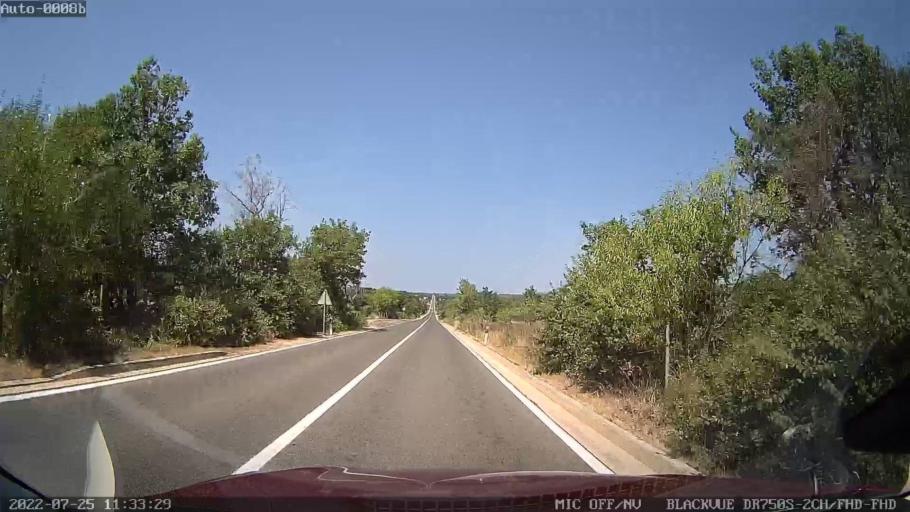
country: HR
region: Zadarska
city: Posedarje
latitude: 44.2263
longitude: 15.4348
